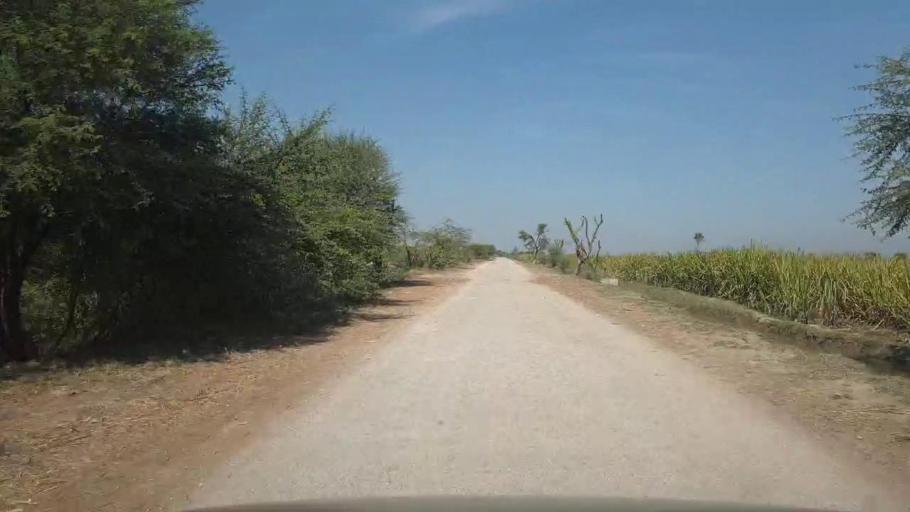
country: PK
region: Sindh
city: Mirwah Gorchani
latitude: 25.4326
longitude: 69.1658
